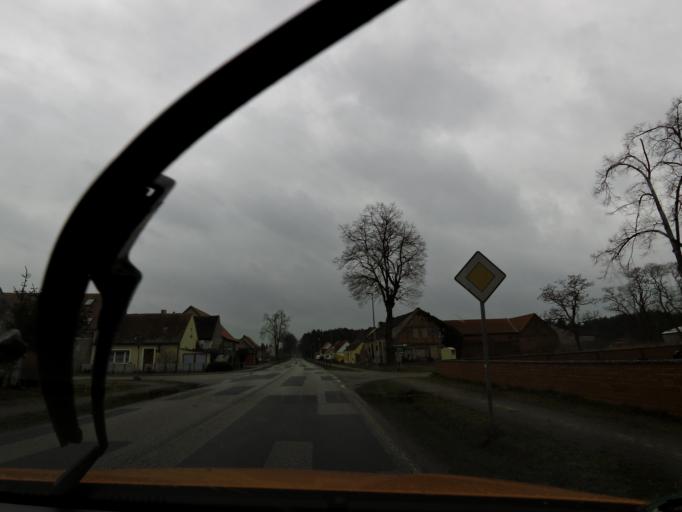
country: DE
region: Brandenburg
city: Ziesar
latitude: 52.2820
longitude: 12.3270
